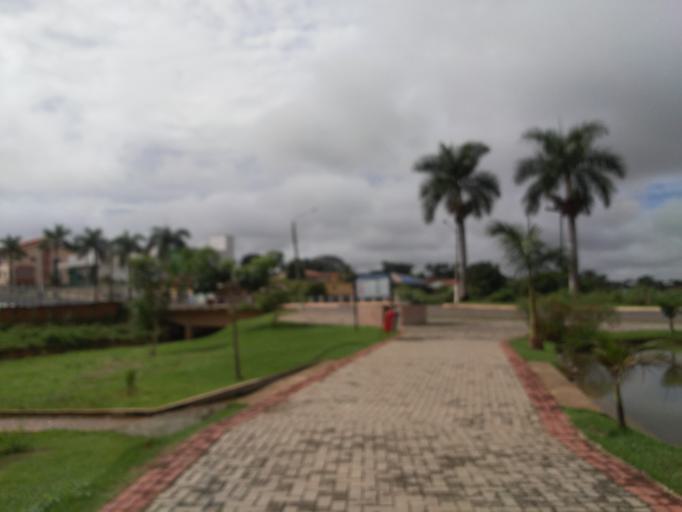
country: BR
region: Goias
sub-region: Ipameri
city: Ipameri
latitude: -17.7203
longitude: -48.1656
